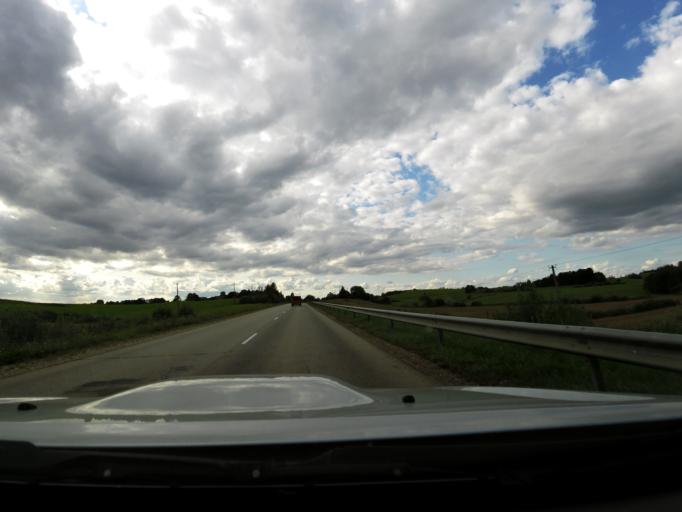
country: LV
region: Ilukste
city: Ilukste
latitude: 55.9750
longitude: 26.0187
